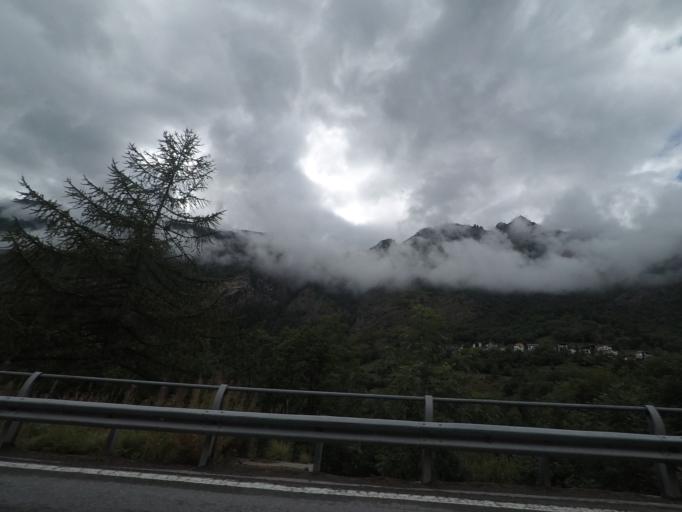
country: IT
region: Aosta Valley
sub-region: Valle d'Aosta
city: Valtournenche
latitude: 45.8684
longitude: 7.6200
